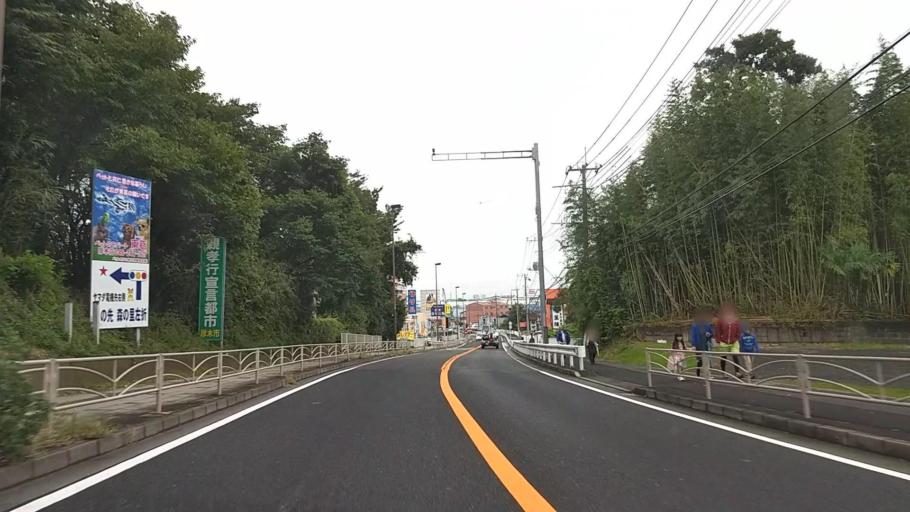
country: JP
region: Kanagawa
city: Atsugi
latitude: 35.4214
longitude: 139.3470
